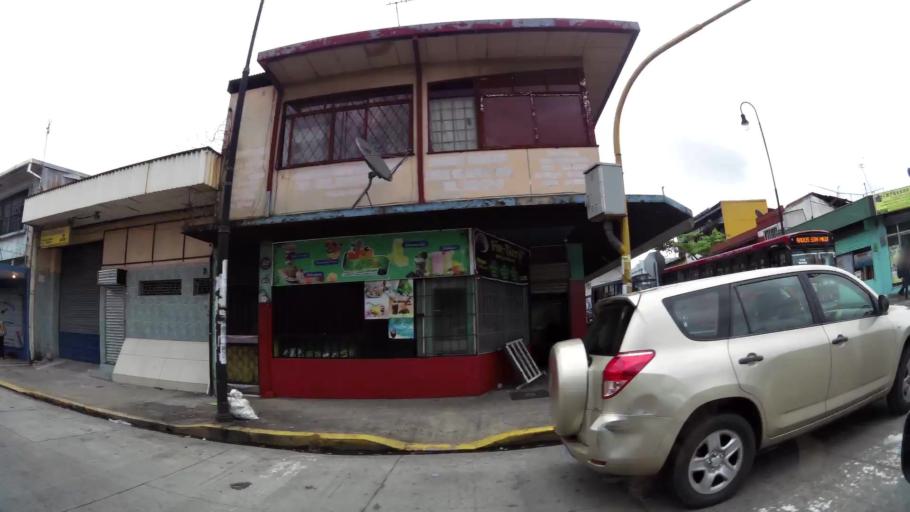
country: CR
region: San Jose
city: San Jose
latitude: 9.9296
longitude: -84.0762
